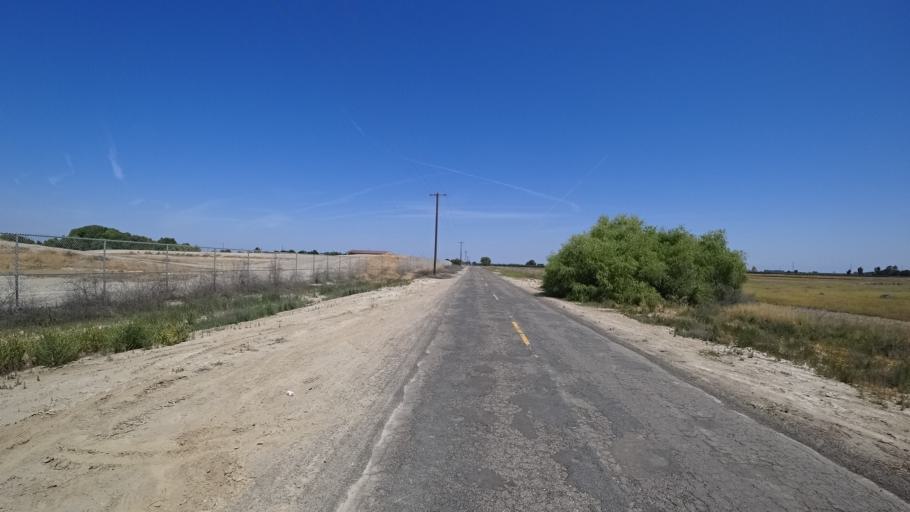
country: US
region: California
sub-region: Kings County
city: Lemoore
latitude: 36.2367
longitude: -119.7446
